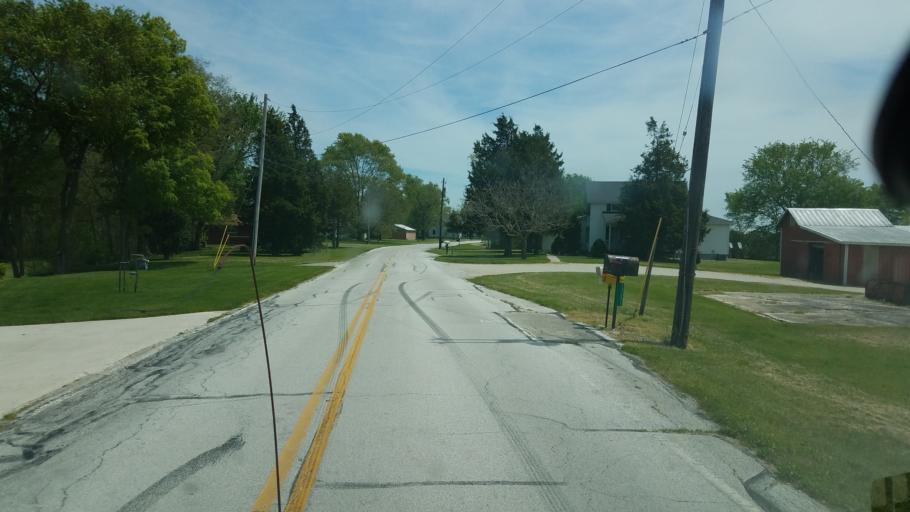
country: US
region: Ohio
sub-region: Ottawa County
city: Oak Harbor
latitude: 41.4959
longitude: -83.1952
